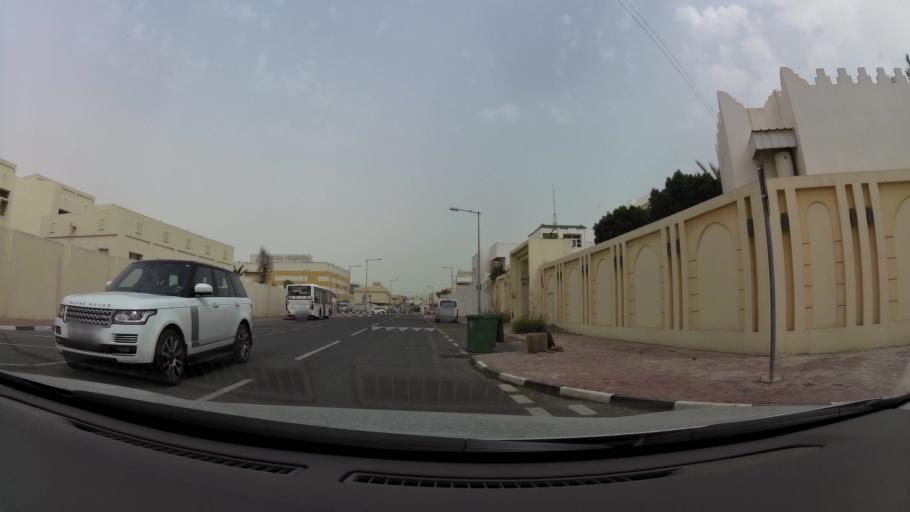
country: QA
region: Baladiyat ad Dawhah
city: Doha
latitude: 25.2577
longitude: 51.5276
